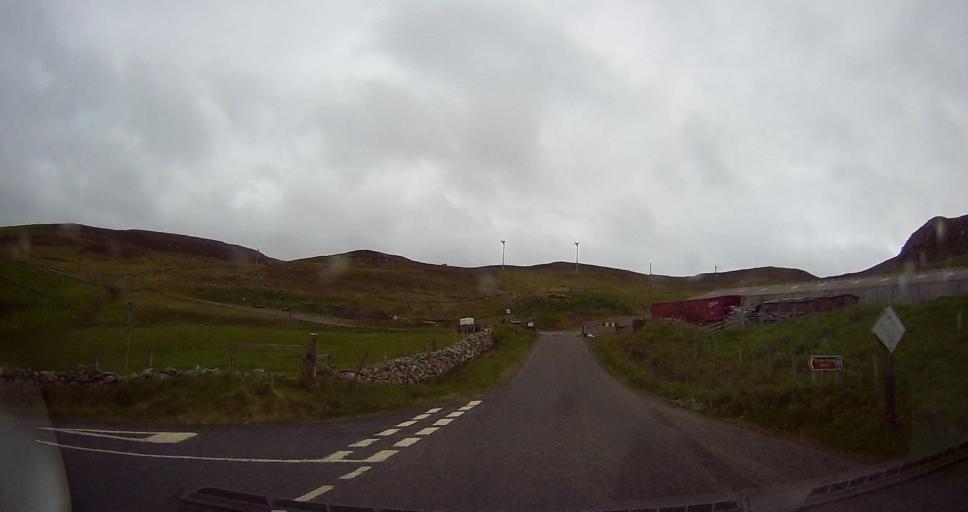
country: GB
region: Scotland
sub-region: Shetland Islands
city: Lerwick
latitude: 60.3860
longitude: -1.3767
